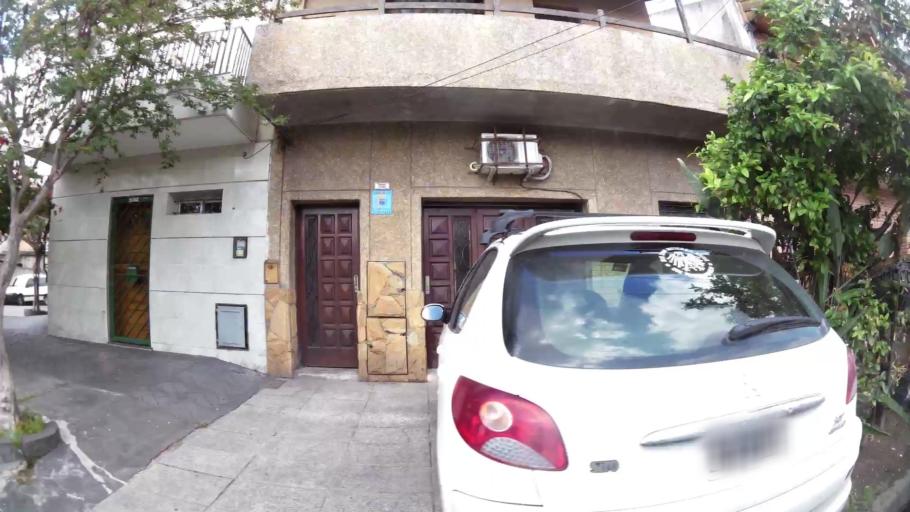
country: AR
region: Buenos Aires
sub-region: Partido de Lanus
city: Lanus
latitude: -34.6879
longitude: -58.4156
